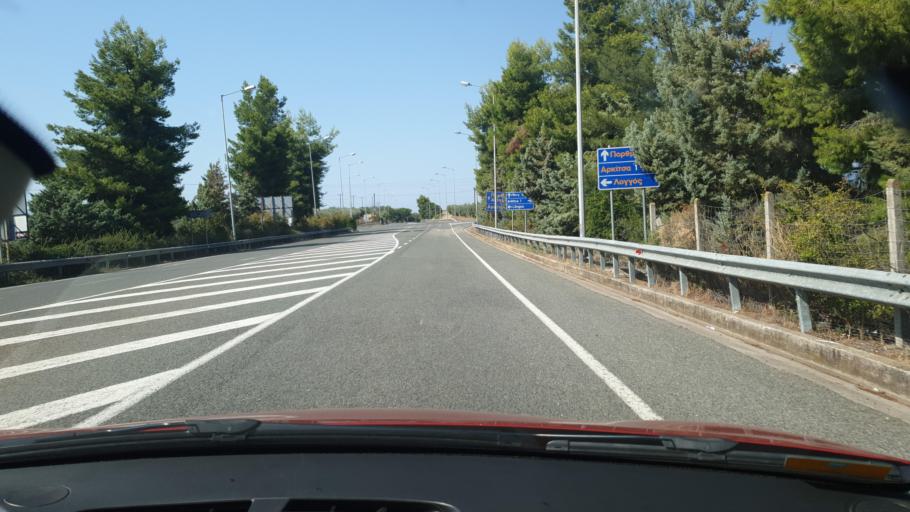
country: GR
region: Central Greece
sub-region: Nomos Fthiotidos
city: Livanates
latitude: 38.7397
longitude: 23.0268
